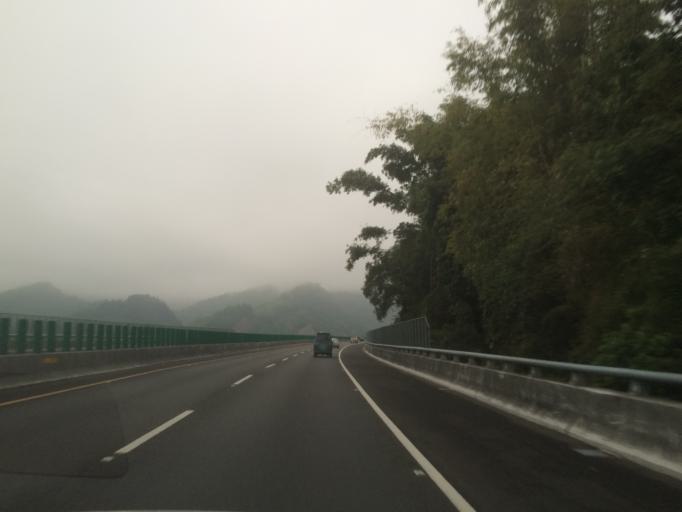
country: TW
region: Taiwan
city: Zhongxing New Village
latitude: 23.9848
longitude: 120.7777
